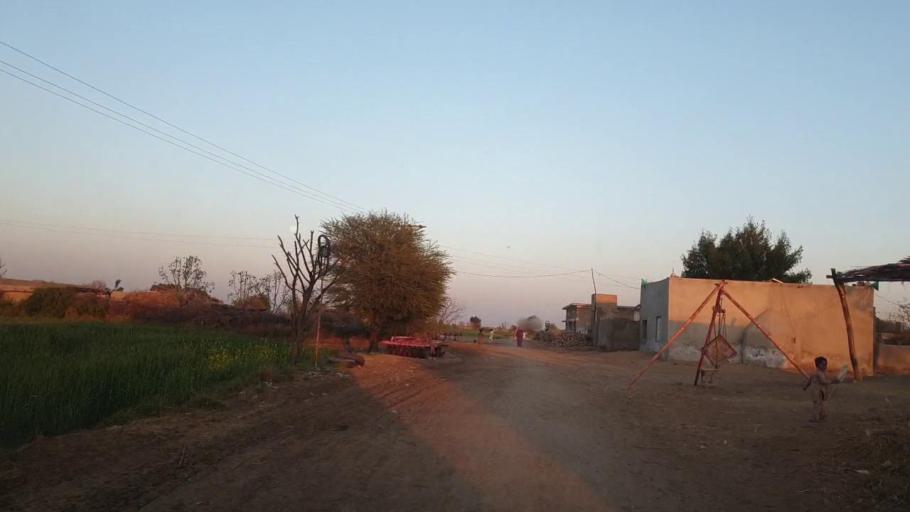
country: PK
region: Sindh
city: Mirpur Khas
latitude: 25.6992
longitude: 69.0532
